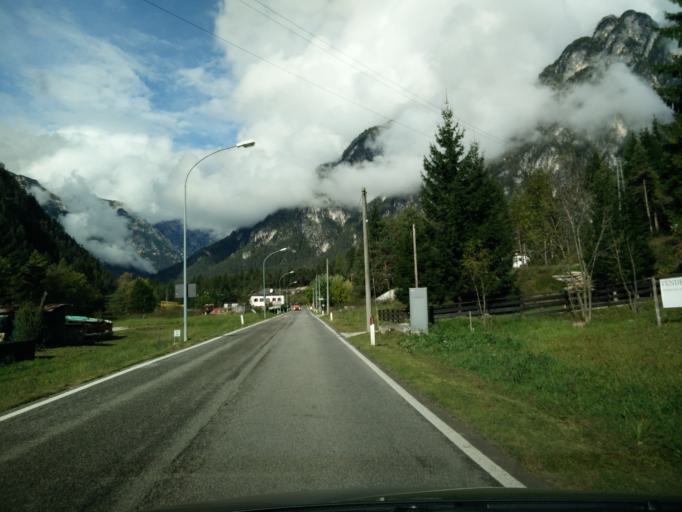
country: IT
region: Veneto
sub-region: Provincia di Belluno
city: Auronzo
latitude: 46.5733
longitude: 12.3947
